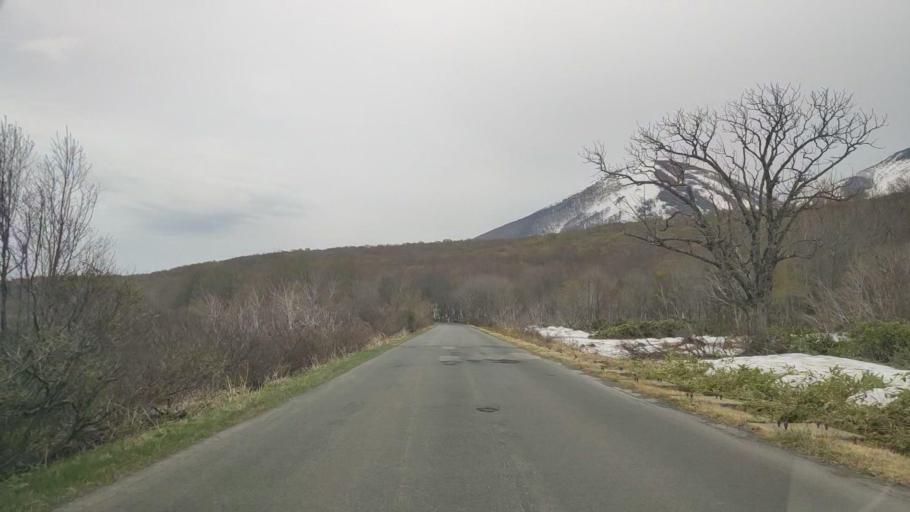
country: JP
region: Aomori
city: Aomori Shi
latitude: 40.6857
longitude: 140.9259
